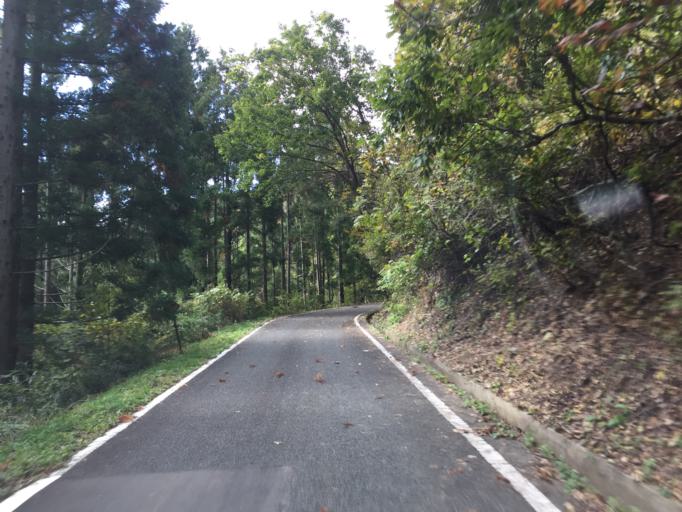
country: JP
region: Fukushima
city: Nihommatsu
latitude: 37.6764
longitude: 140.3840
